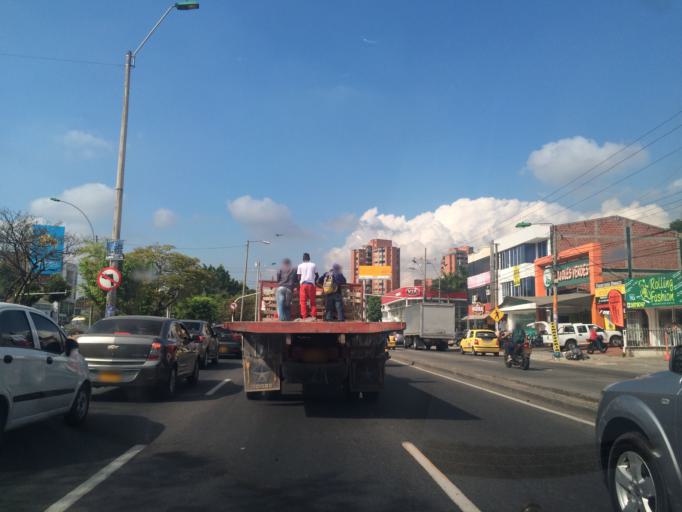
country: CO
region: Valle del Cauca
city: Cali
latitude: 3.3989
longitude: -76.5425
